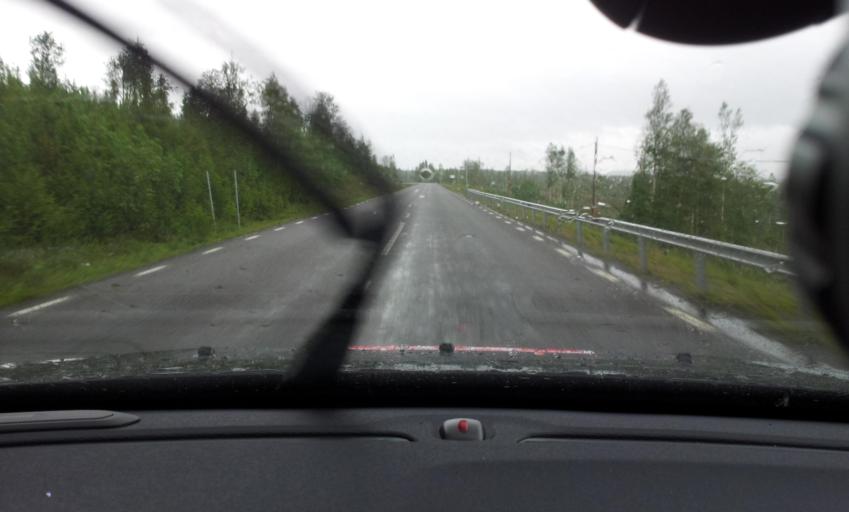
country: SE
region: Jaemtland
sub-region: Are Kommun
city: Are
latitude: 63.2170
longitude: 13.0802
